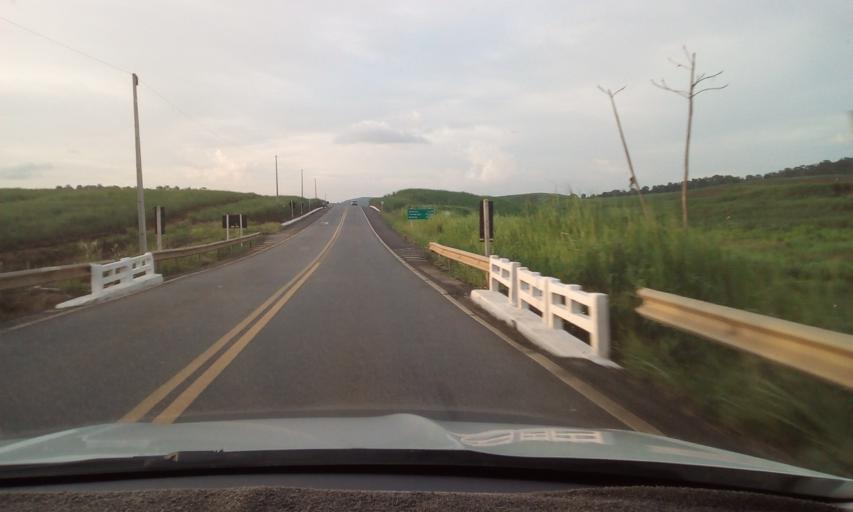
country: BR
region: Pernambuco
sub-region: Vicencia
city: Vicencia
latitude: -7.6523
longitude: -35.2510
